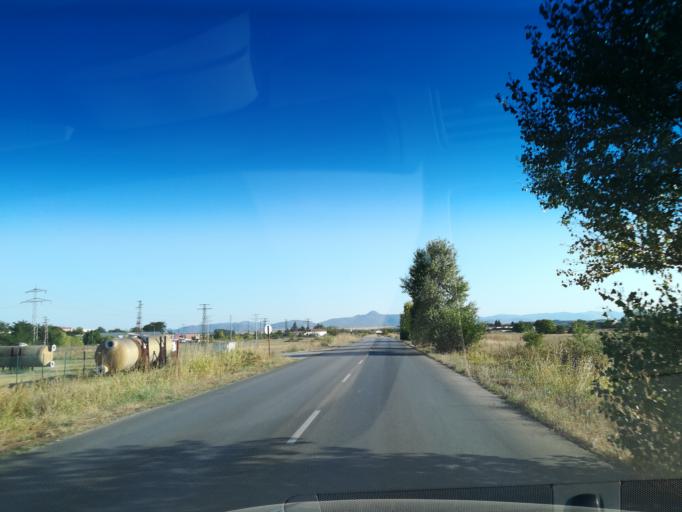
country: BG
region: Stara Zagora
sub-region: Obshtina Chirpan
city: Chirpan
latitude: 42.0955
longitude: 25.2105
